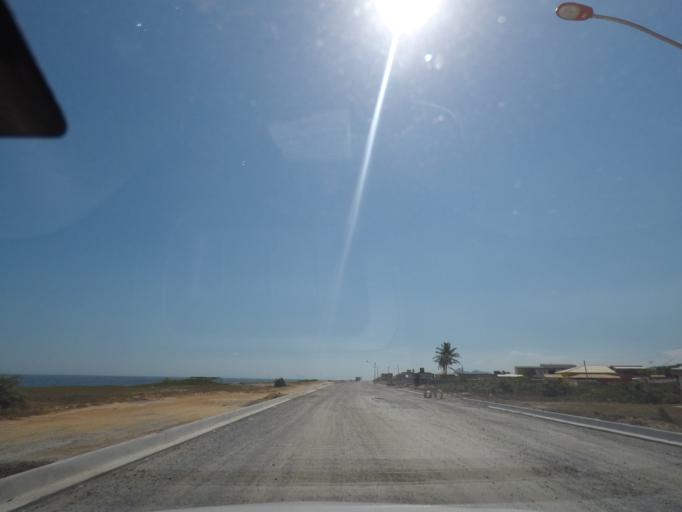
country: BR
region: Rio de Janeiro
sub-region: Marica
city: Marica
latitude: -22.9729
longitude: -42.9093
